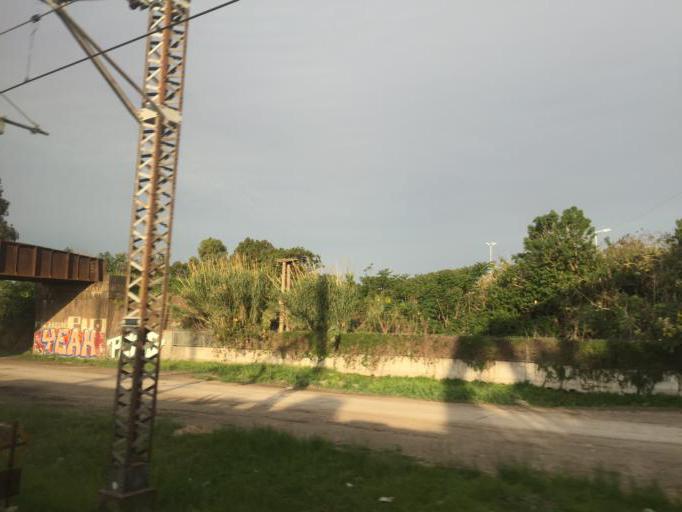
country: AR
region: Buenos Aires
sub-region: Partido de Avellaneda
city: Avellaneda
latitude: -34.6715
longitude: -58.3775
